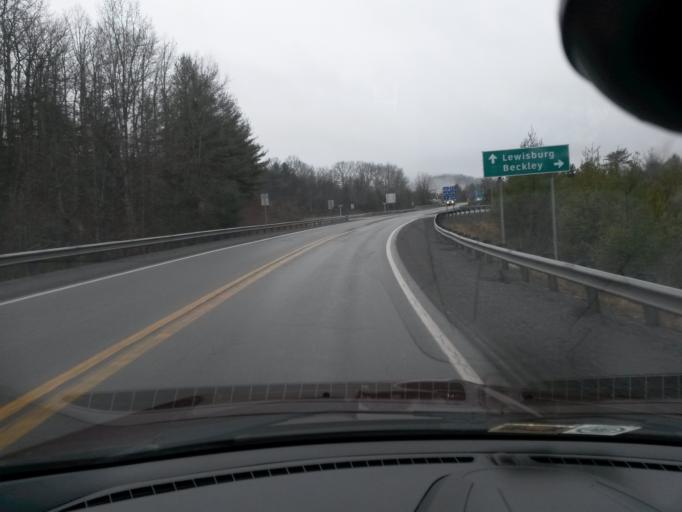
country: US
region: West Virginia
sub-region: Greenbrier County
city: Lewisburg
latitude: 37.8695
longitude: -80.5527
